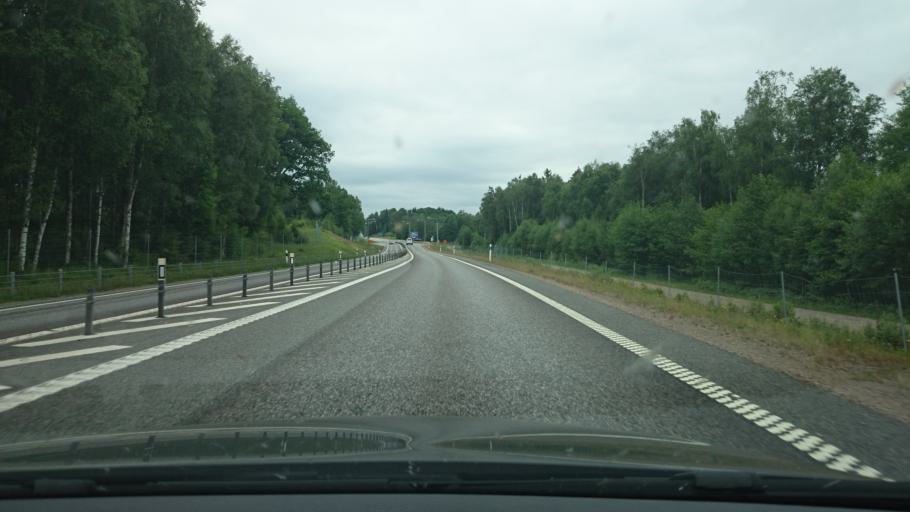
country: SE
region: Halland
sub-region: Hylte Kommun
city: Hyltebruk
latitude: 56.9848
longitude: 13.2134
